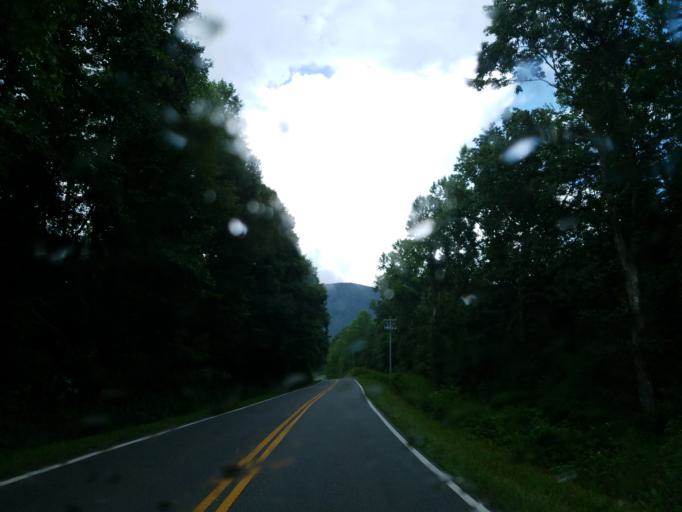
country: US
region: Georgia
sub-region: Gilmer County
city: Ellijay
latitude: 34.6746
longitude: -84.3831
